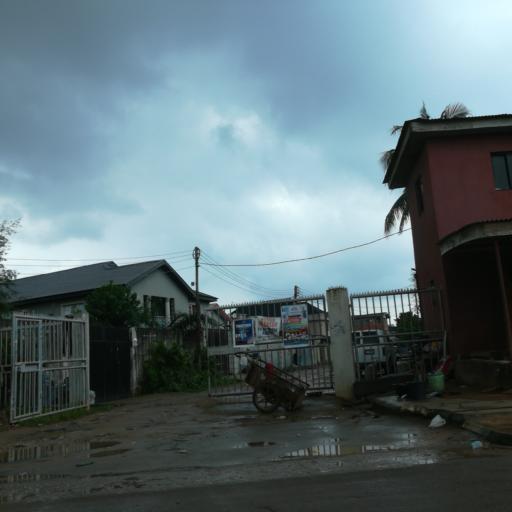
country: NG
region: Lagos
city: Agege
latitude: 6.5899
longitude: 3.2946
